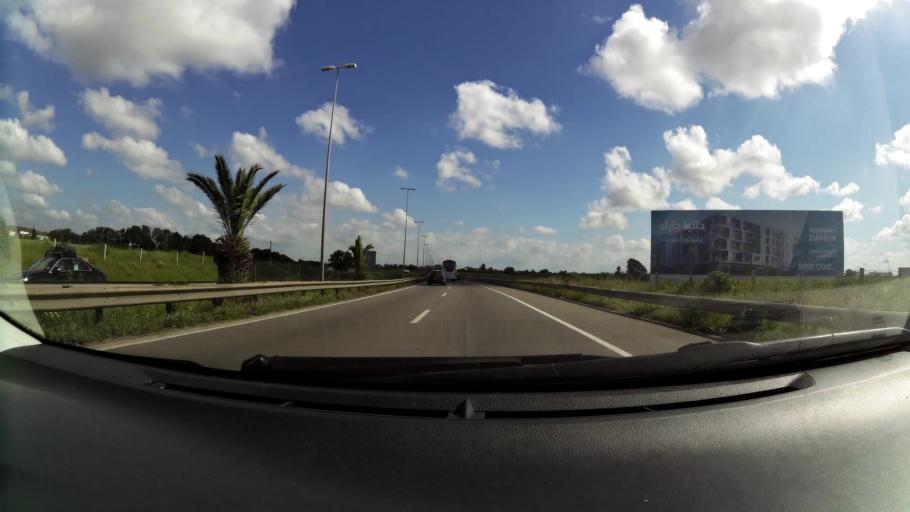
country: MA
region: Grand Casablanca
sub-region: Nouaceur
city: Bouskoura
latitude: 33.4482
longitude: -7.6333
